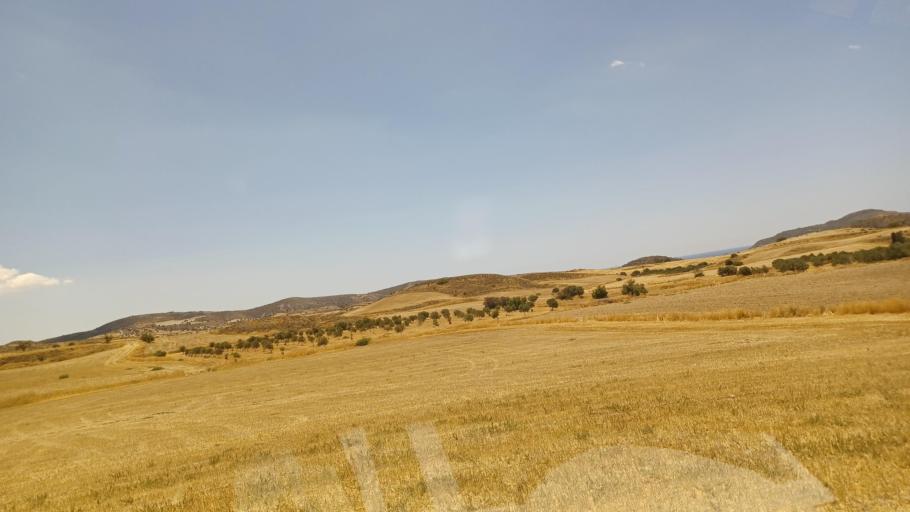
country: CY
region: Larnaka
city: Troulloi
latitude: 35.0360
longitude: 33.6271
